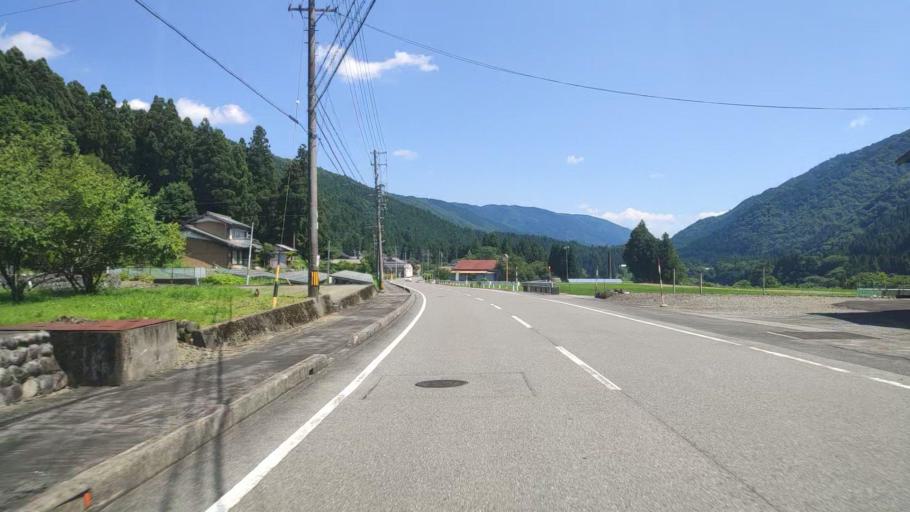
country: JP
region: Gifu
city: Godo
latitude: 35.6494
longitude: 136.5977
